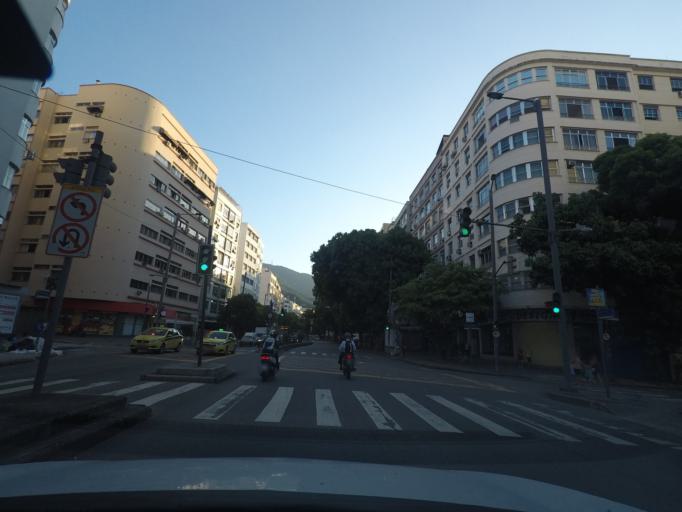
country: BR
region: Rio de Janeiro
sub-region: Rio De Janeiro
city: Rio de Janeiro
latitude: -22.9277
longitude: -43.2362
